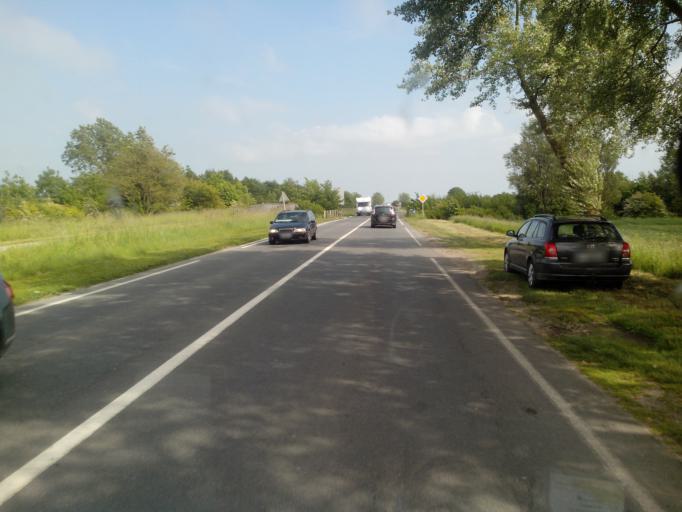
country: FR
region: Picardie
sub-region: Departement de la Somme
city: Le Crotoy
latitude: 50.2229
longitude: 1.6361
